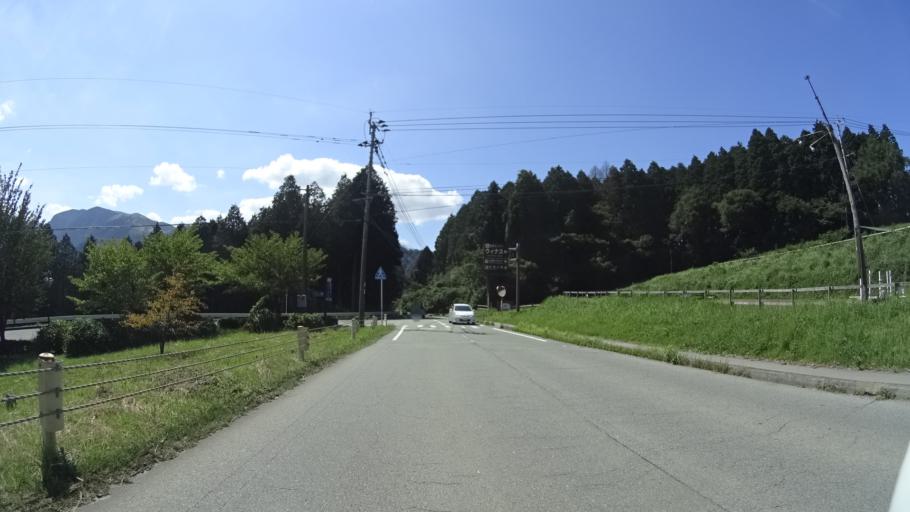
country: JP
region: Kumamoto
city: Aso
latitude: 32.8716
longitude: 131.0031
